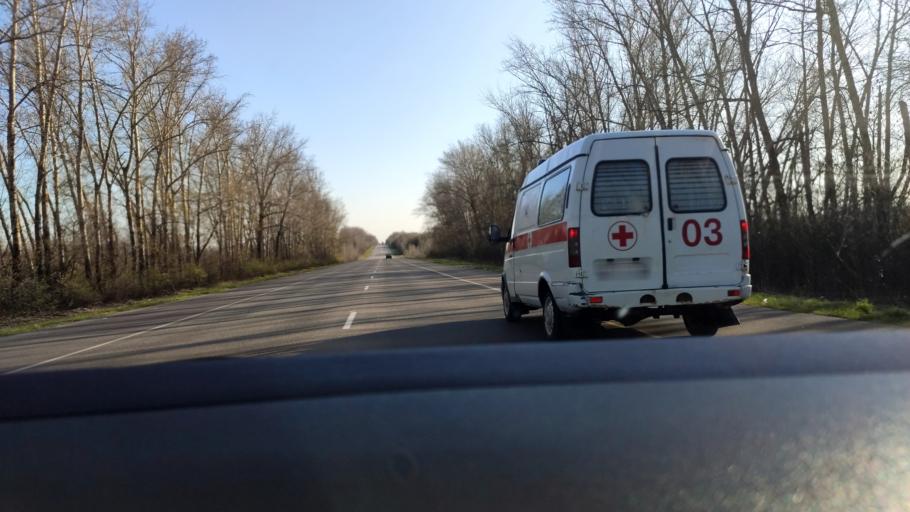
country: RU
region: Voronezj
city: Uryv-Pokrovka
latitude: 51.1596
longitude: 39.0676
